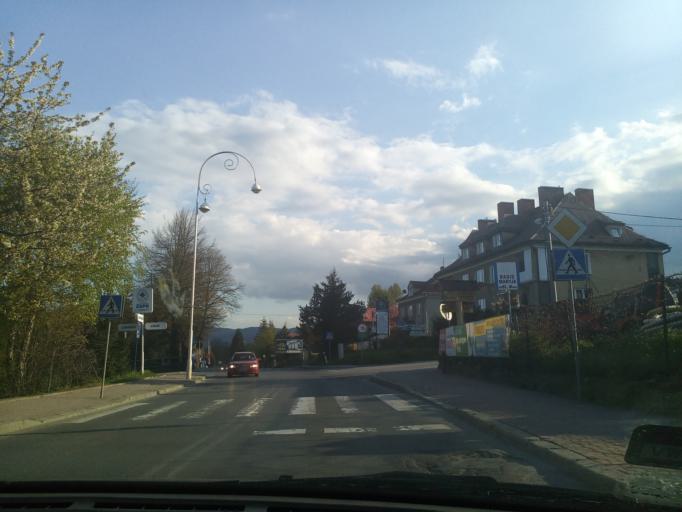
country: PL
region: Lesser Poland Voivodeship
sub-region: Powiat nowosadecki
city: Krynica-Zdroj
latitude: 49.4065
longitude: 20.9532
